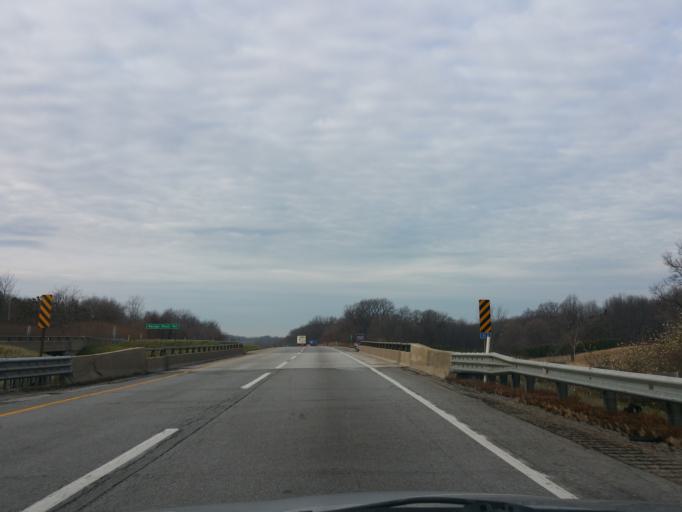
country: US
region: Indiana
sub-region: LaPorte County
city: LaPorte
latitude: 41.6747
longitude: -86.6993
